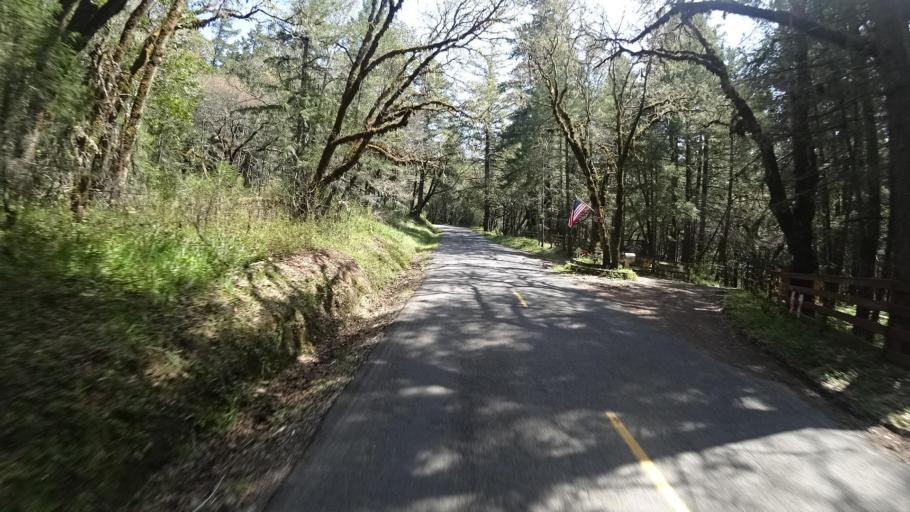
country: US
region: California
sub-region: Humboldt County
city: Redway
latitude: 40.2822
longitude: -123.6450
